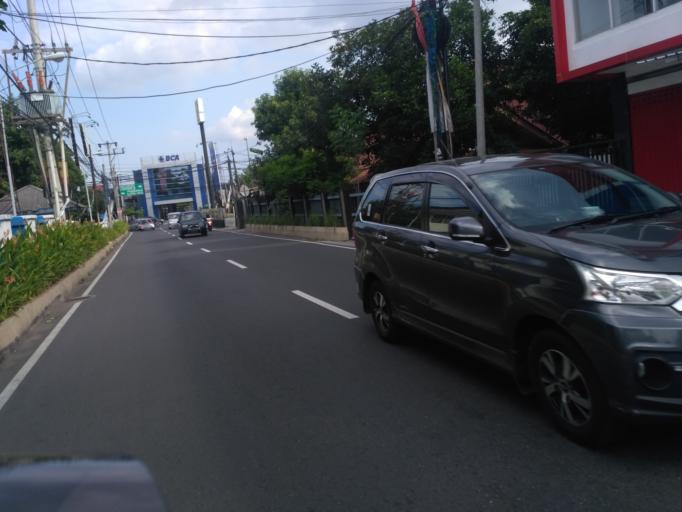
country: ID
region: Daerah Istimewa Yogyakarta
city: Depok
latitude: -7.7824
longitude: 110.4084
